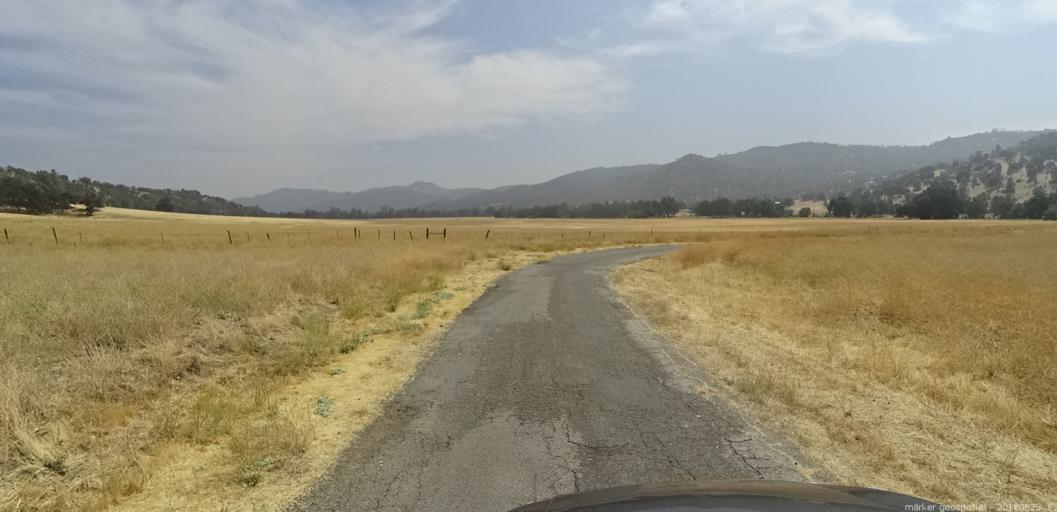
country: US
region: California
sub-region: Fresno County
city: Coalinga
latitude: 36.1991
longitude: -120.7047
